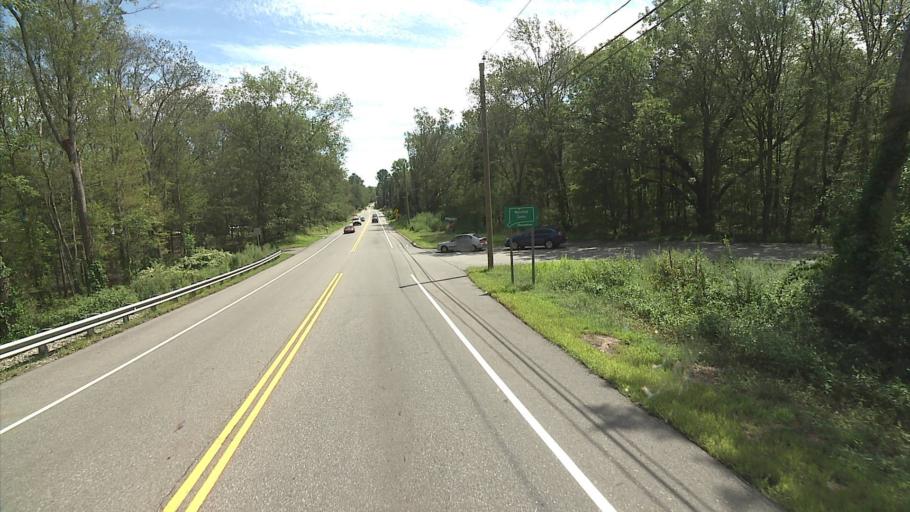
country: US
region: Connecticut
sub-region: Tolland County
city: Mansfield City
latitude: 41.7720
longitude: -72.2048
